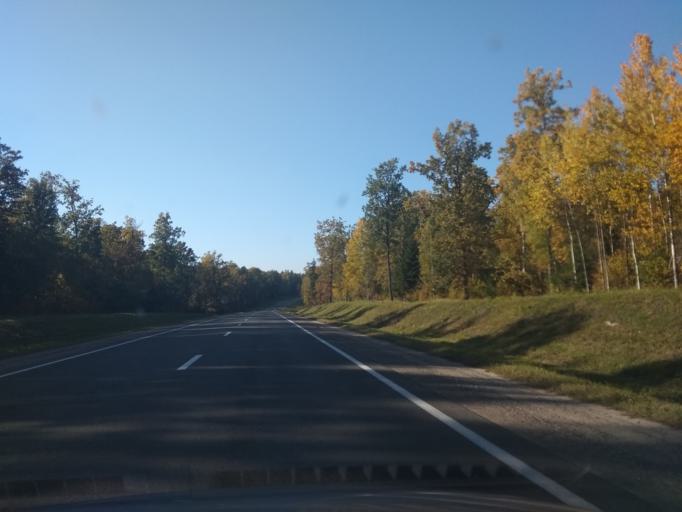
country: BY
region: Grodnenskaya
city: Slonim
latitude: 53.0586
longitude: 25.2979
